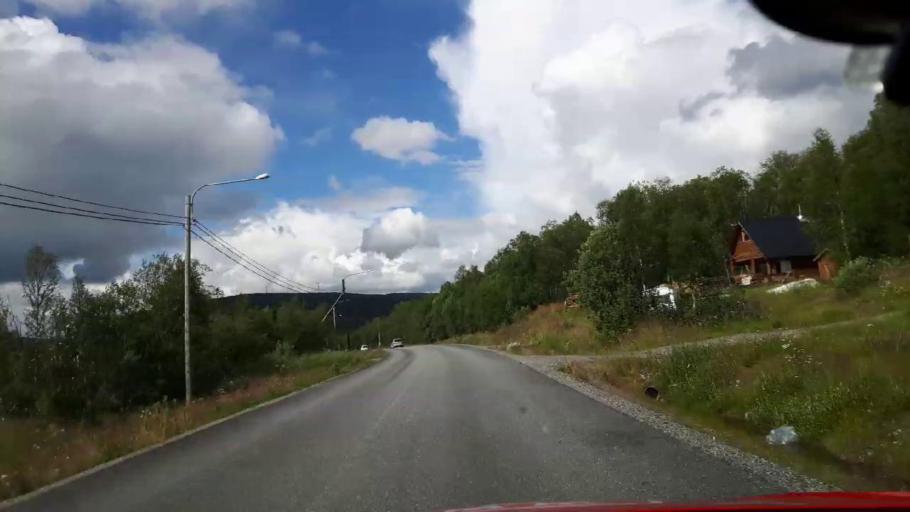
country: NO
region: Nordland
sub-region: Hattfjelldal
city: Hattfjelldal
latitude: 65.0641
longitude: 14.8511
